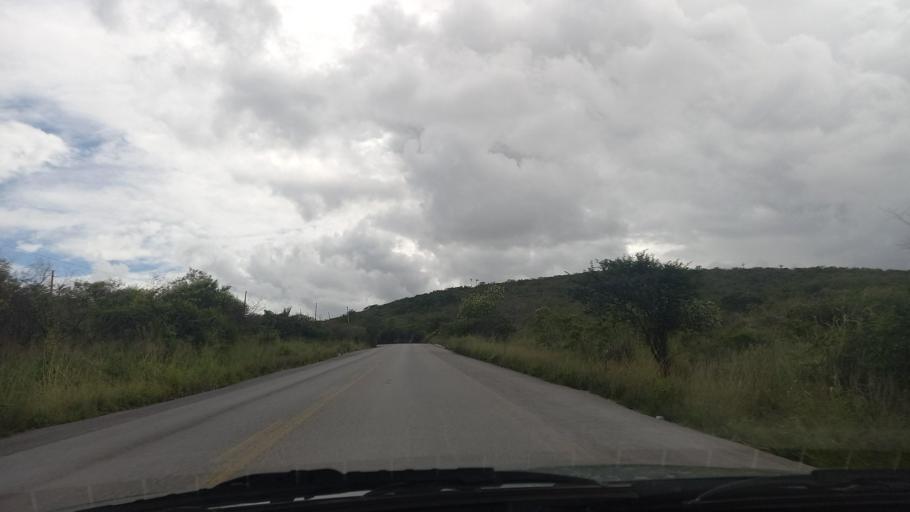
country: BR
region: Pernambuco
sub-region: Lajedo
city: Lajedo
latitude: -8.6733
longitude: -36.3967
